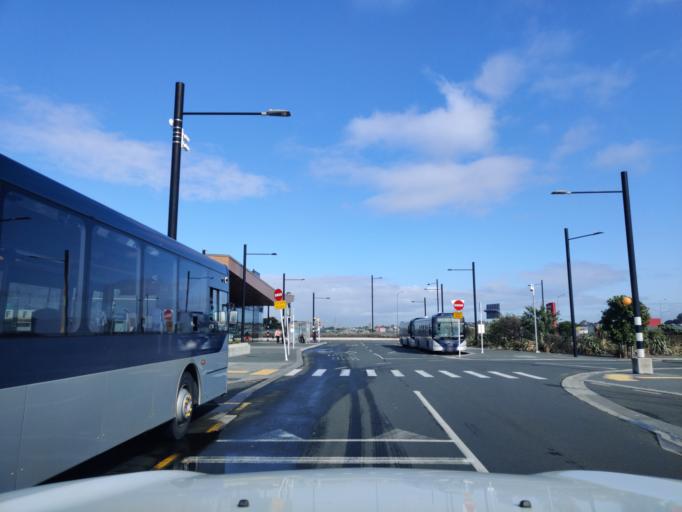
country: NZ
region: Auckland
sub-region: Auckland
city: Tamaki
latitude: -36.8976
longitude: 174.8495
